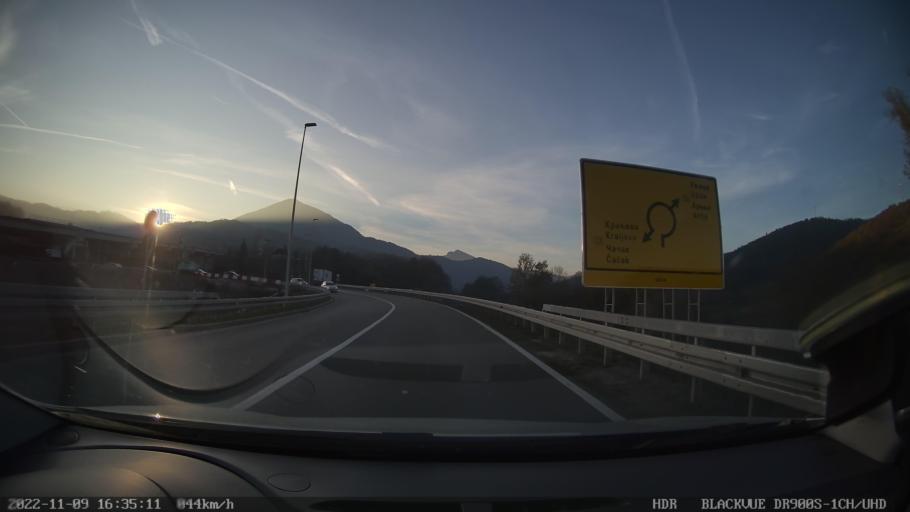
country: RS
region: Central Serbia
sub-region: Moravicki Okrug
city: Cacak
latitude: 43.9031
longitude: 20.2605
